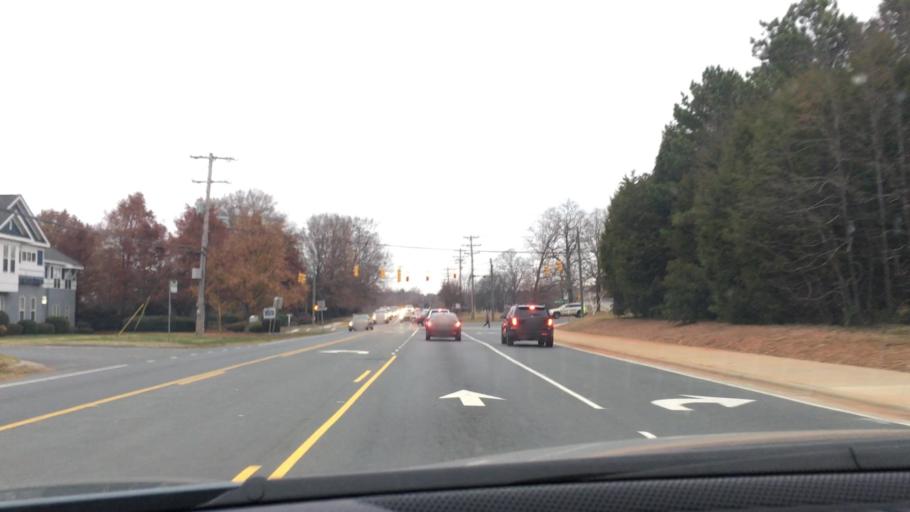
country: US
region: North Carolina
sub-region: Mecklenburg County
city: Cornelius
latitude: 35.4604
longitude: -80.8886
